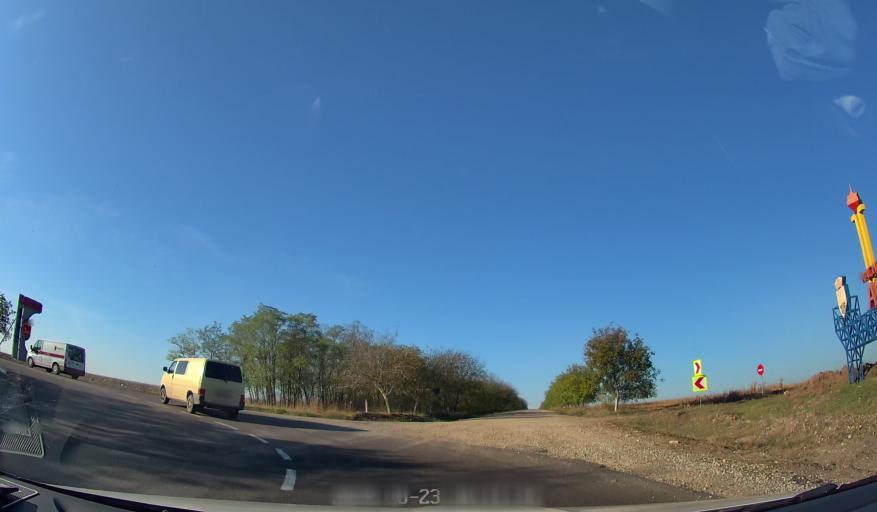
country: MD
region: Anenii Noi
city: Anenii Noi
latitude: 46.7613
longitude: 29.2517
